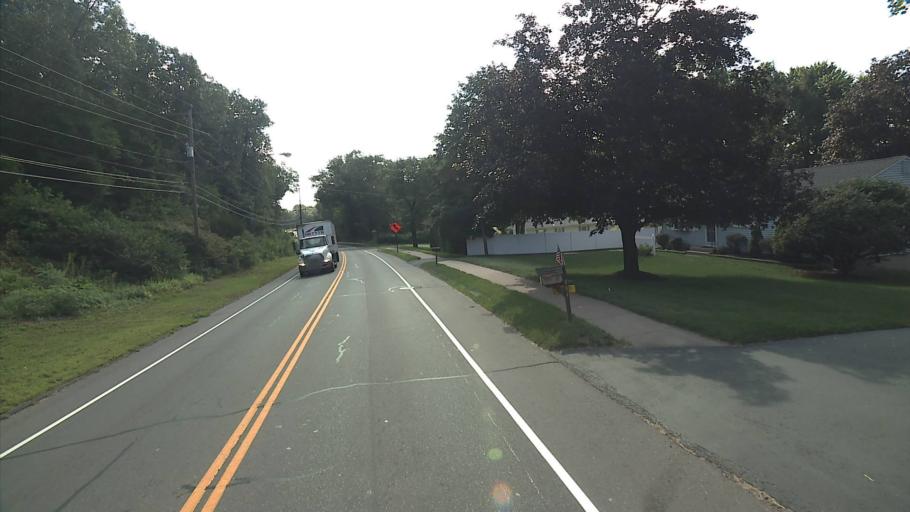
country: US
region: Connecticut
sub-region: Hartford County
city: Hazardville
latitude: 41.9847
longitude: -72.5225
